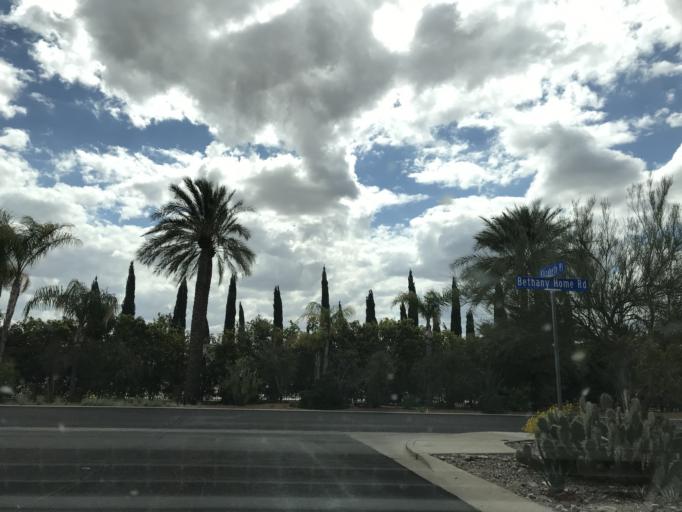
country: US
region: Arizona
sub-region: Maricopa County
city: Paradise Valley
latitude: 33.5248
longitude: -112.0025
